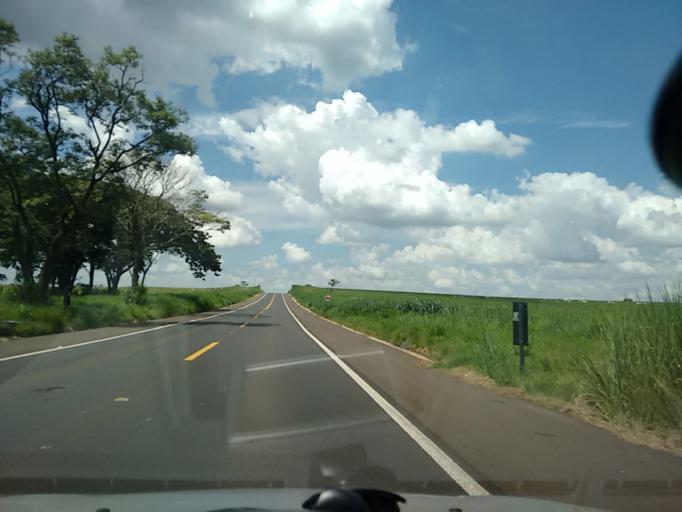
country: BR
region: Sao Paulo
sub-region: Osvaldo Cruz
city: Osvaldo Cruz
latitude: -21.8742
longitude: -50.8582
